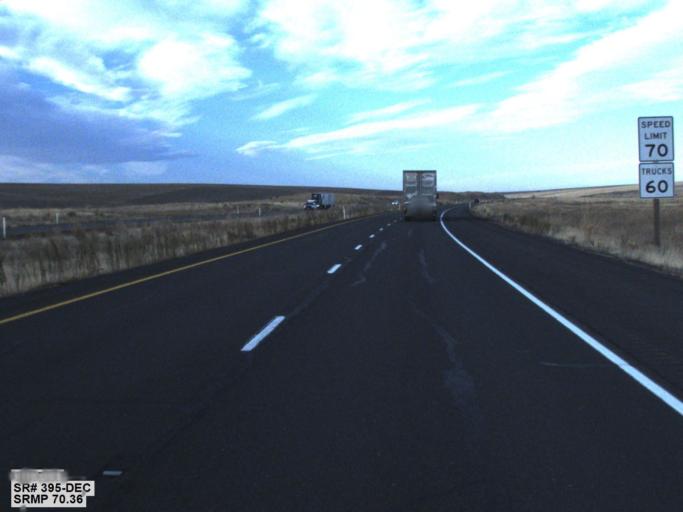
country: US
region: Washington
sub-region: Franklin County
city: Connell
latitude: 46.8214
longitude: -118.6788
